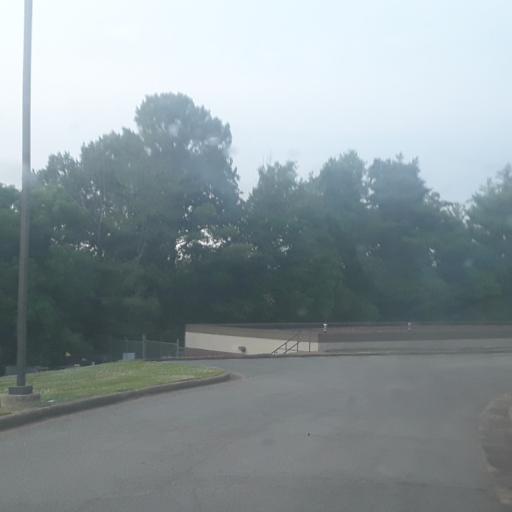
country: US
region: Tennessee
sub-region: Davidson County
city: Oak Hill
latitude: 36.0656
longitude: -86.7433
